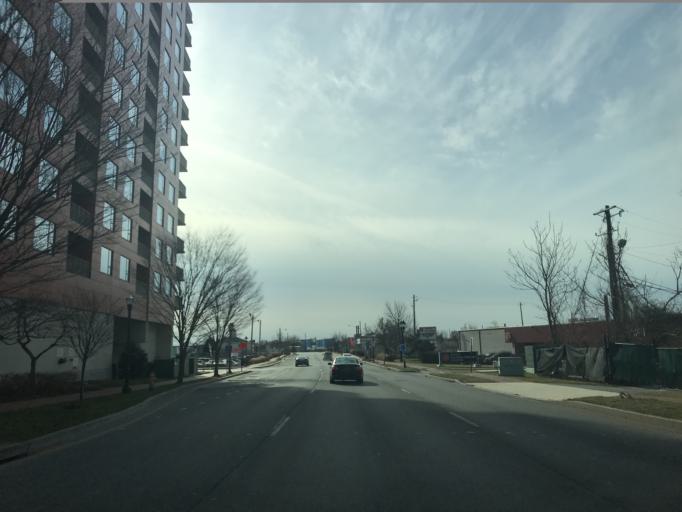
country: US
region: Delaware
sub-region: New Castle County
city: Wilmington
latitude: 39.7358
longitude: -75.5545
